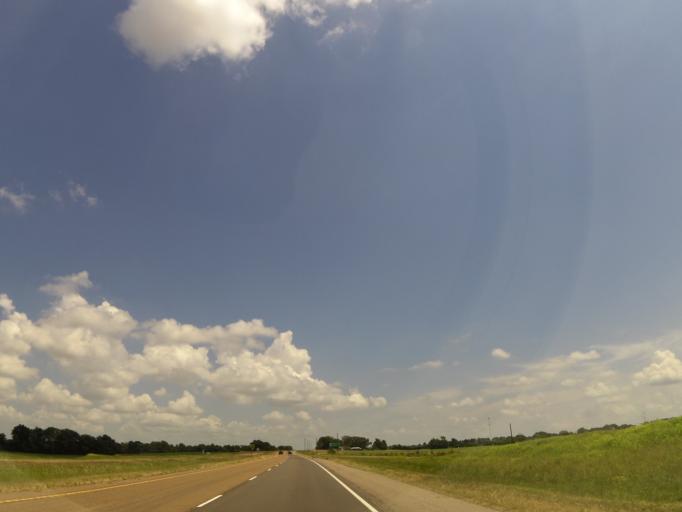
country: US
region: Tennessee
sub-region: Dyer County
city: Dyersburg
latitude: 35.9552
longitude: -89.3197
